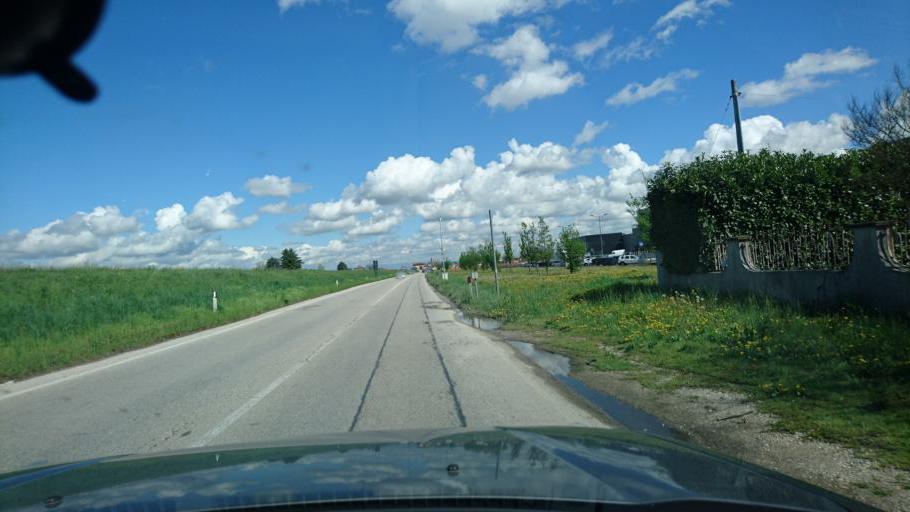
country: IT
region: Veneto
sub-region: Provincia di Padova
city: Mejaniga
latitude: 45.4770
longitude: 11.8980
